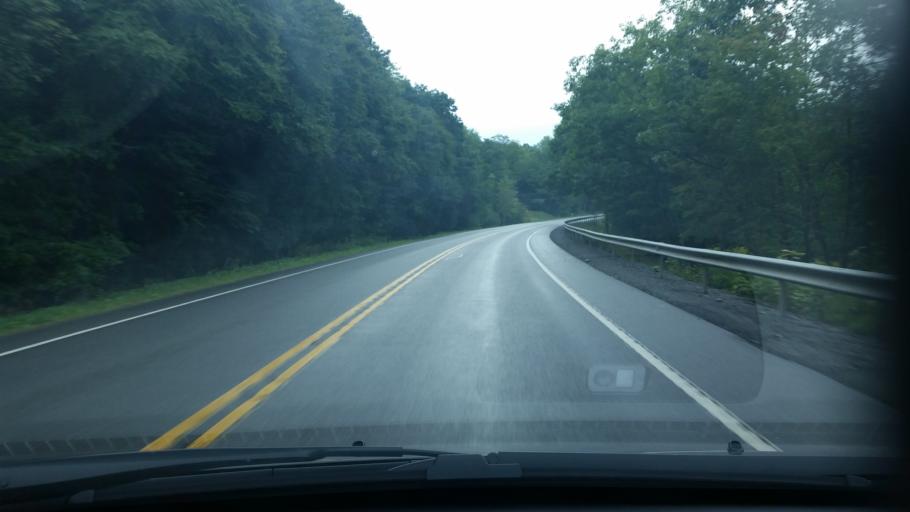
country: US
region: Pennsylvania
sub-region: Clearfield County
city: Shiloh
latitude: 41.0854
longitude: -78.2553
